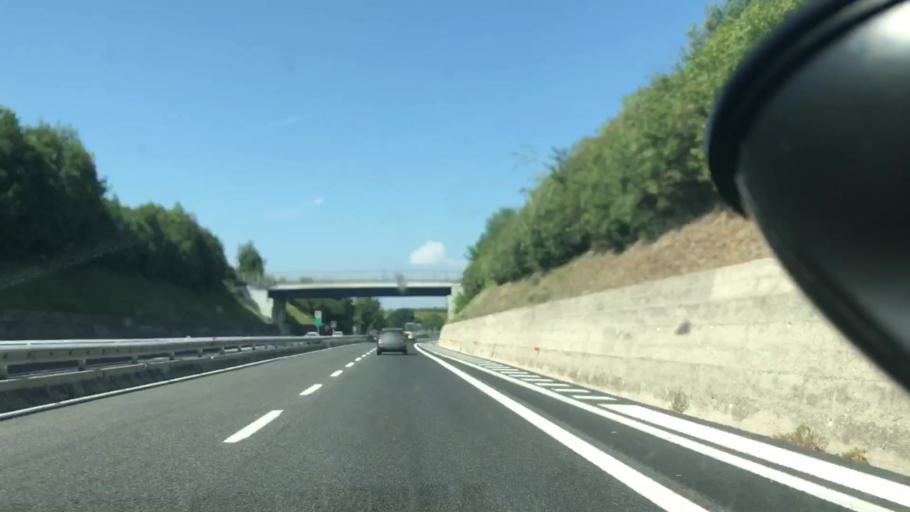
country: IT
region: Abruzzo
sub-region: Provincia di Chieti
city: Ortona
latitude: 42.3373
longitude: 14.3628
